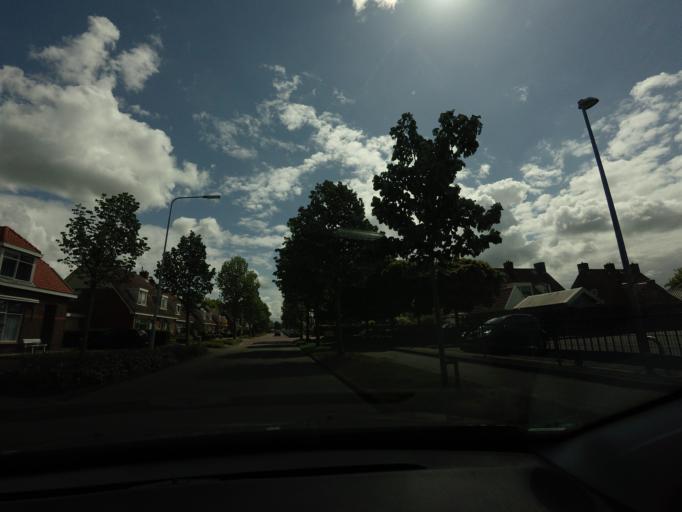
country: NL
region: Friesland
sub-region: Gemeente Gaasterlan-Sleat
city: Balk
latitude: 52.8985
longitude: 5.5761
